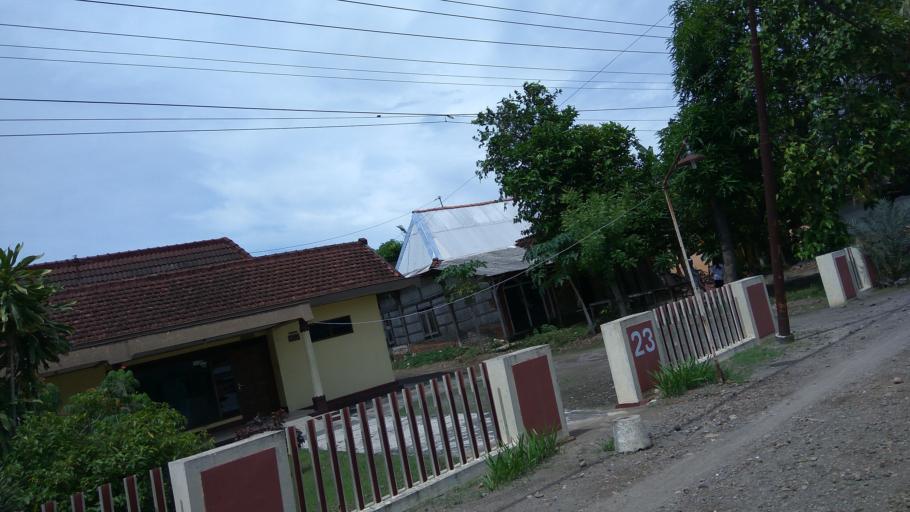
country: ID
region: Central Java
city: Mranggen
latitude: -7.0507
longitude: 110.6248
